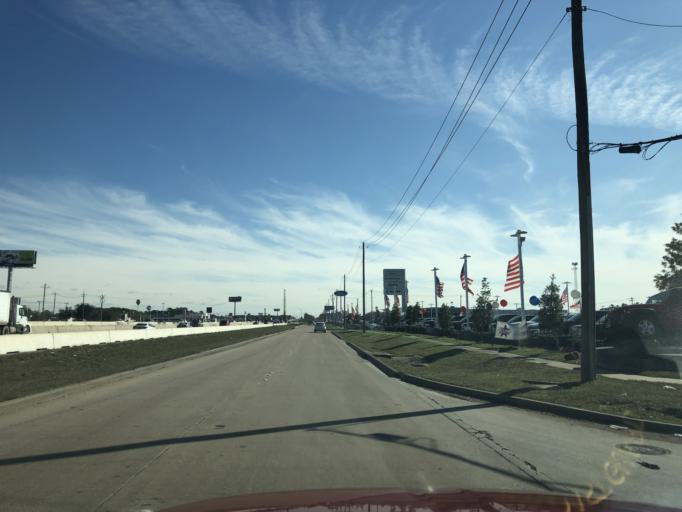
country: US
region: Texas
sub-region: Galveston County
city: Dickinson
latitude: 29.4579
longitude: -95.0846
